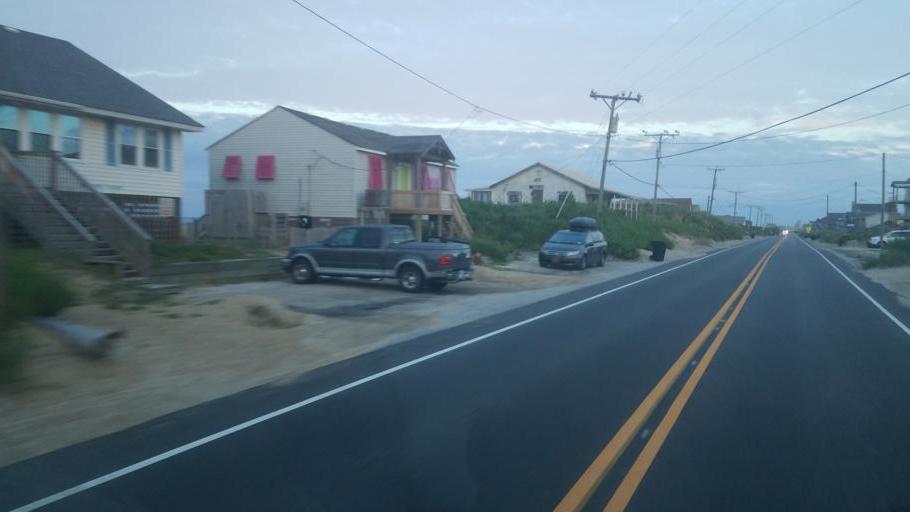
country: US
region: North Carolina
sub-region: Dare County
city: Kitty Hawk
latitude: 36.0627
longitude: -75.6877
